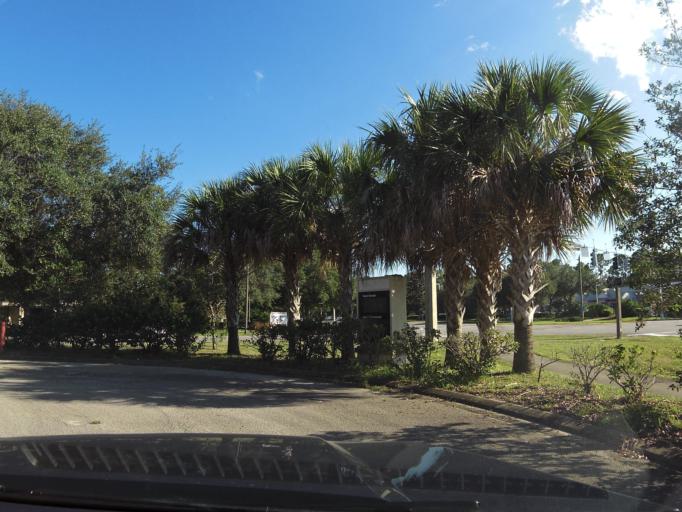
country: US
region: Florida
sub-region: Flagler County
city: Palm Coast
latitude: 29.5507
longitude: -81.2365
